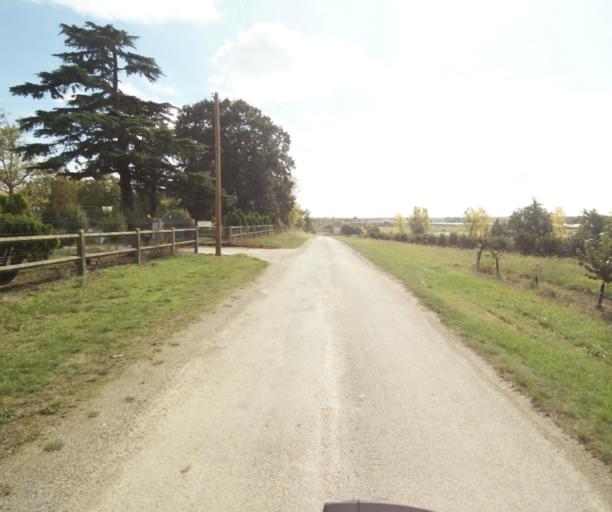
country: FR
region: Midi-Pyrenees
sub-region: Departement du Tarn-et-Garonne
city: Montech
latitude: 43.9497
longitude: 1.2075
